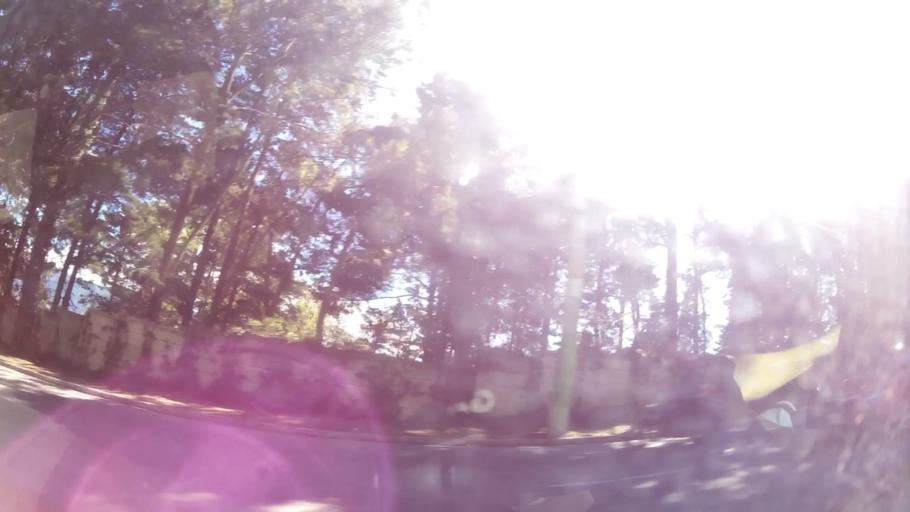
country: GT
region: Guatemala
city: San Jose Pinula
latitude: 14.5464
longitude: -90.4198
